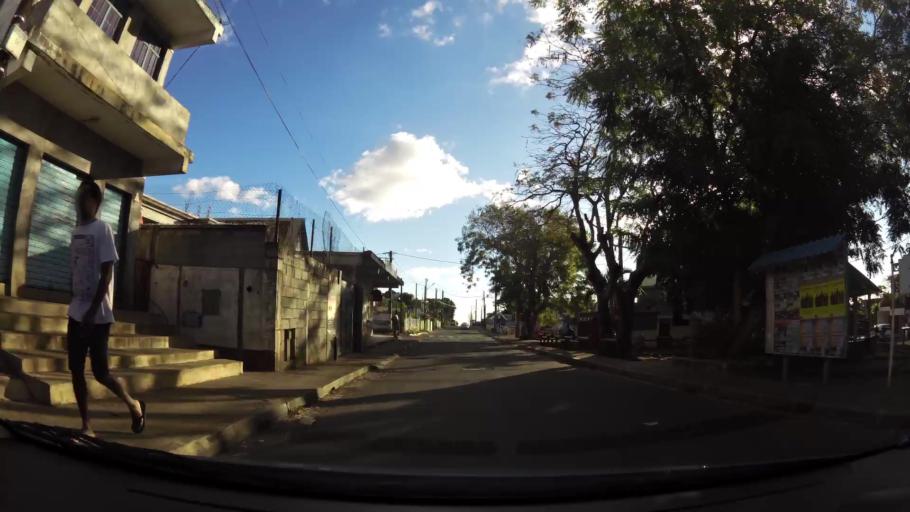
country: MU
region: Black River
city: Petite Riviere
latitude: -20.2145
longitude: 57.4668
